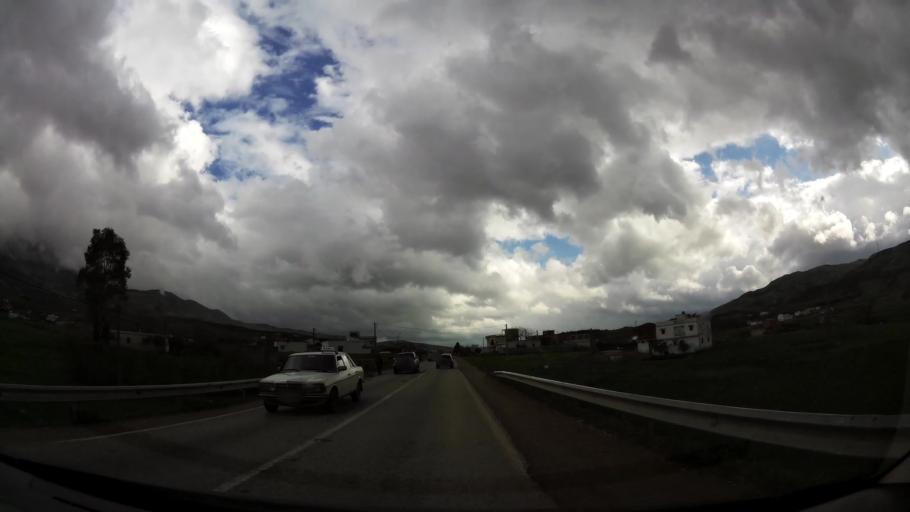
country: MA
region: Tanger-Tetouan
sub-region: Tetouan
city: Zinat
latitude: 35.3163
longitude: -5.3557
